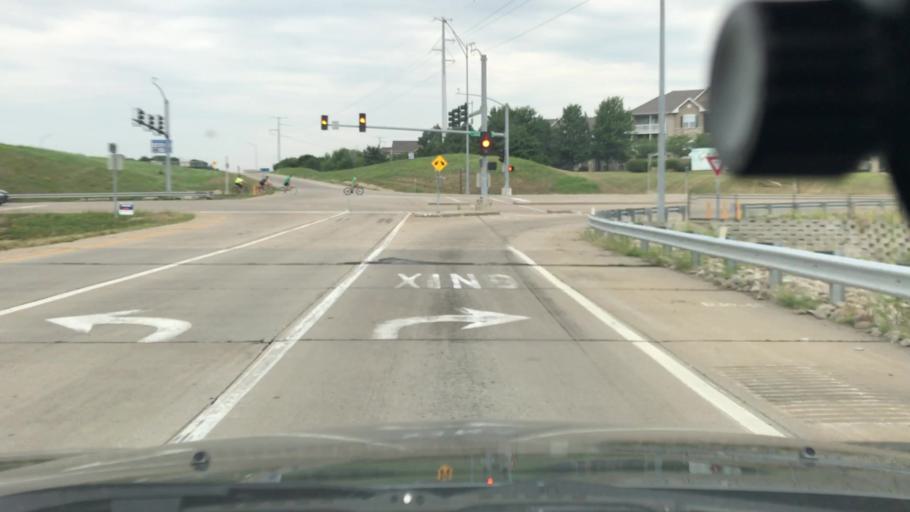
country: US
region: Missouri
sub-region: Saint Charles County
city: Saint Charles
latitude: 38.7440
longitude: -90.5286
